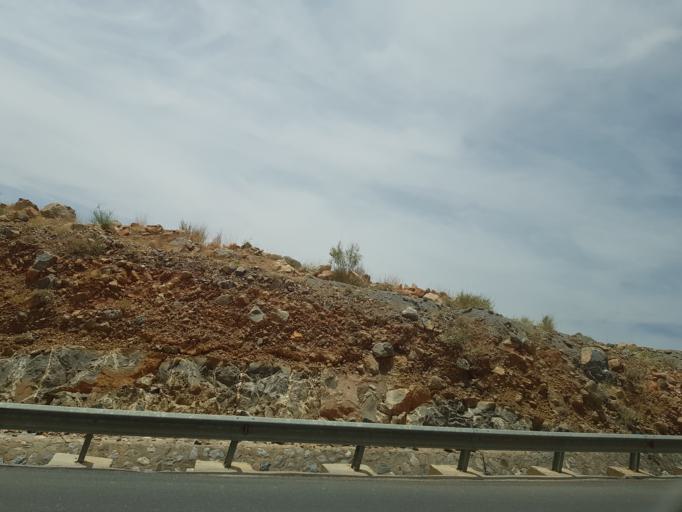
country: OM
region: Muhafazat ad Dakhiliyah
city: Izki
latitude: 22.9808
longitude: 57.7019
